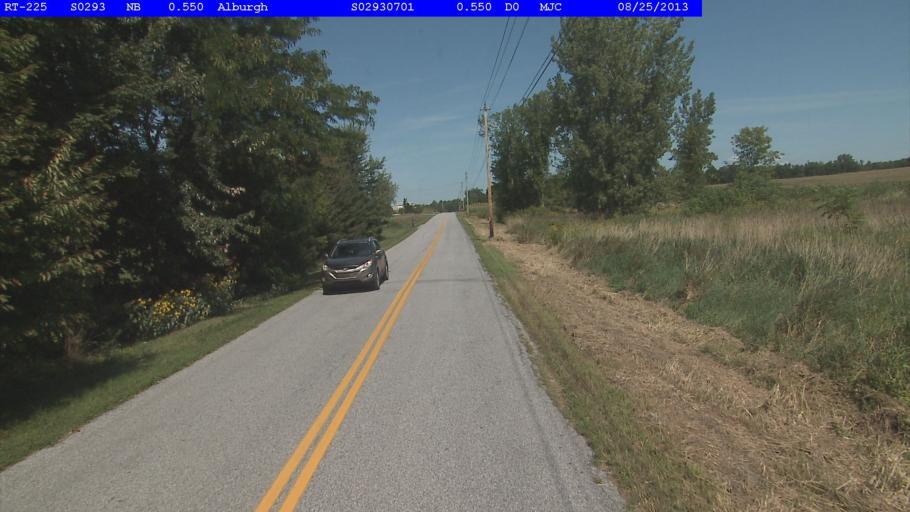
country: US
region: New York
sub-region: Clinton County
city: Rouses Point
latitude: 44.9967
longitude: -73.2961
